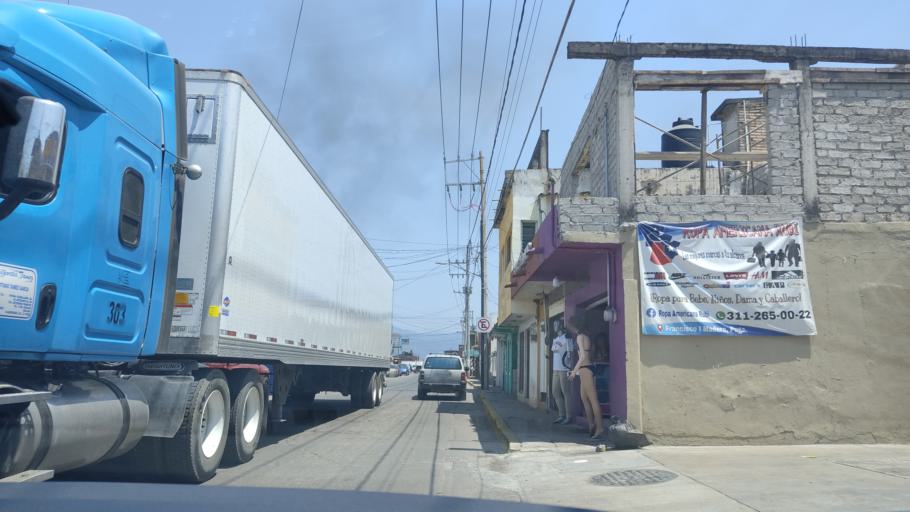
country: MX
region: Nayarit
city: Puga
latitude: 21.5822
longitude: -104.8240
